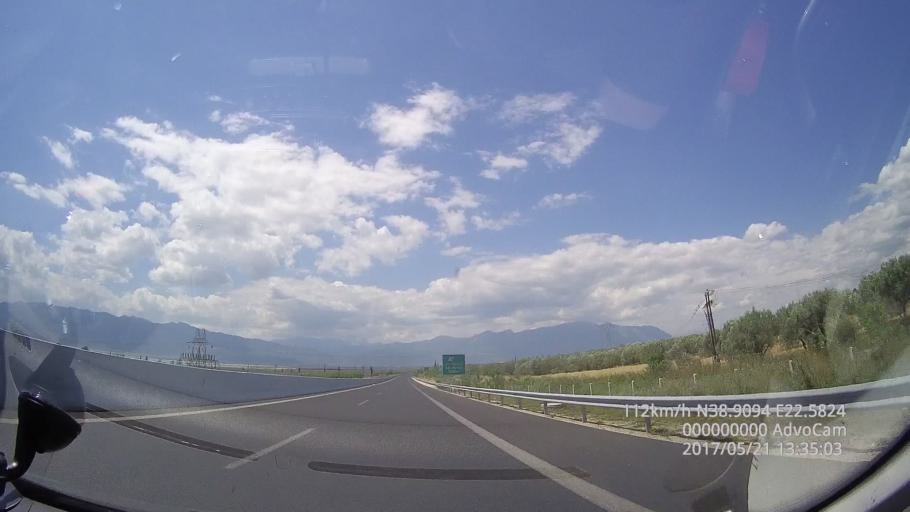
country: GR
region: Central Greece
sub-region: Nomos Fthiotidos
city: Stylida
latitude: 38.9093
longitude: 22.5823
